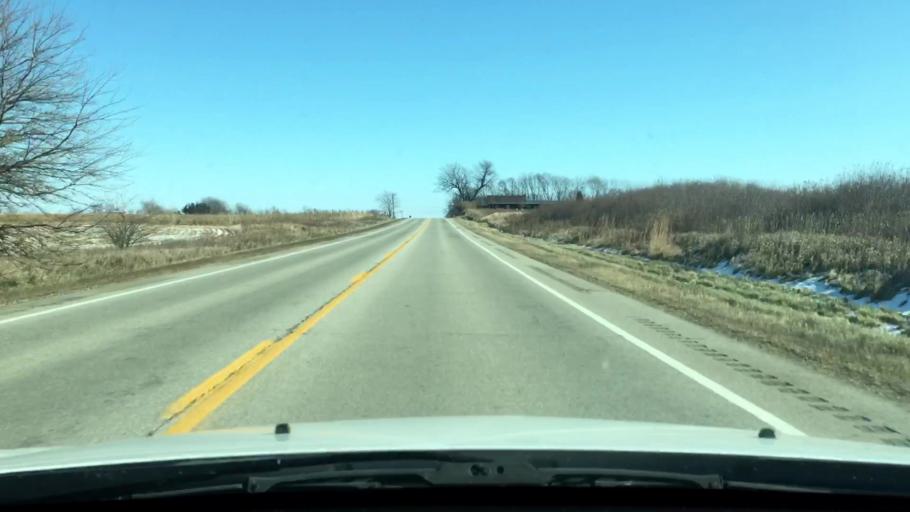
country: US
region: Illinois
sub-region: DeKalb County
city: Malta
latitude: 42.0009
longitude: -88.9044
